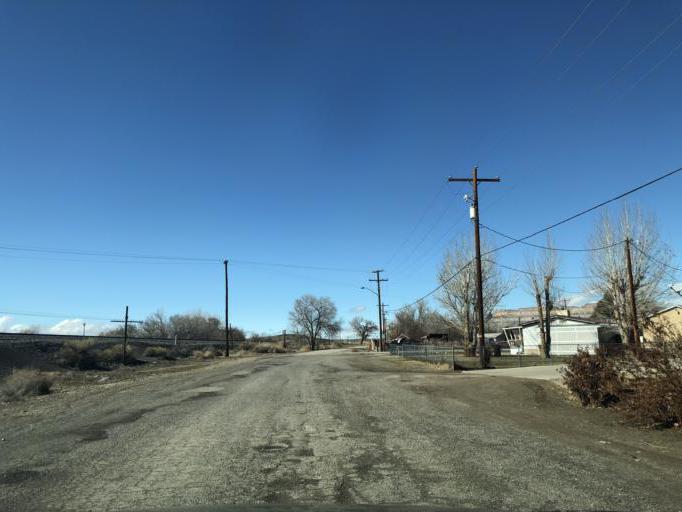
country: US
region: Utah
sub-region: Carbon County
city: East Carbon City
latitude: 38.9869
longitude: -110.1571
